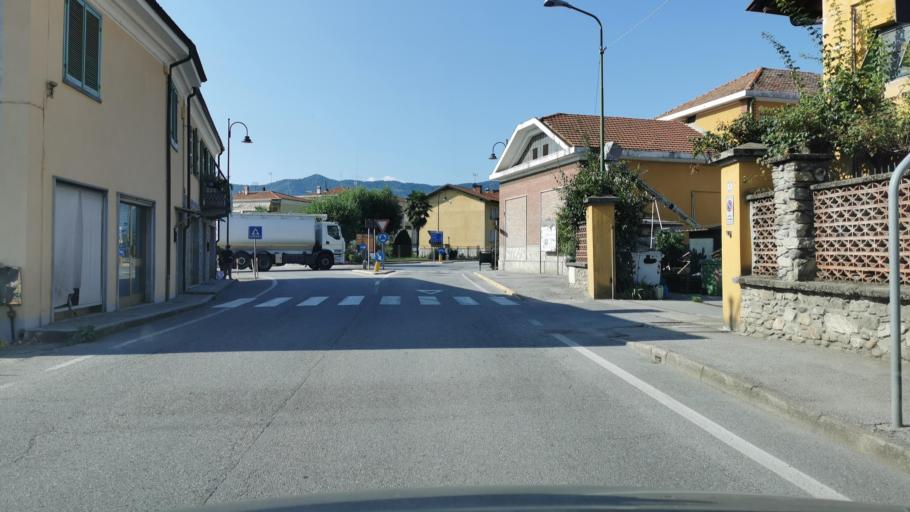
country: IT
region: Piedmont
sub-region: Provincia di Cuneo
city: Revello
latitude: 44.6572
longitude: 7.3929
